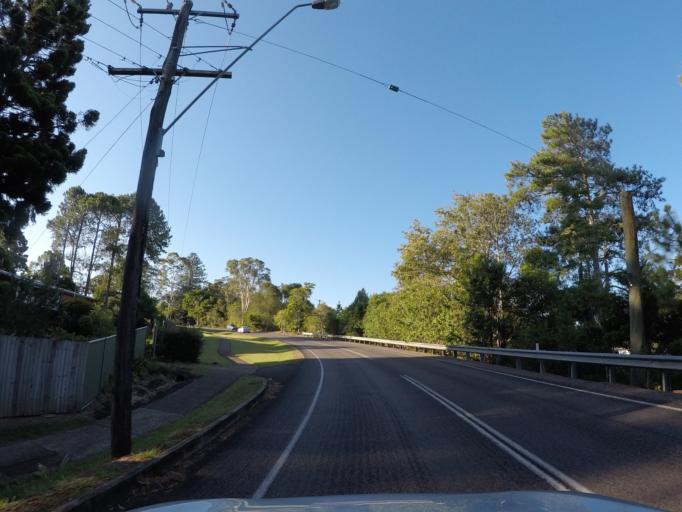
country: AU
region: Queensland
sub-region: Sunshine Coast
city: Nambour
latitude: -26.6343
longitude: 152.8703
